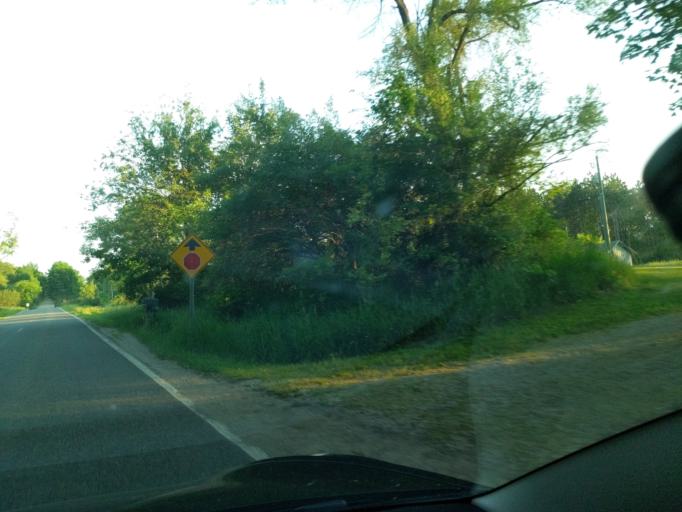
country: US
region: Michigan
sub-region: Barry County
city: Nashville
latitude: 42.5397
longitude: -85.0937
